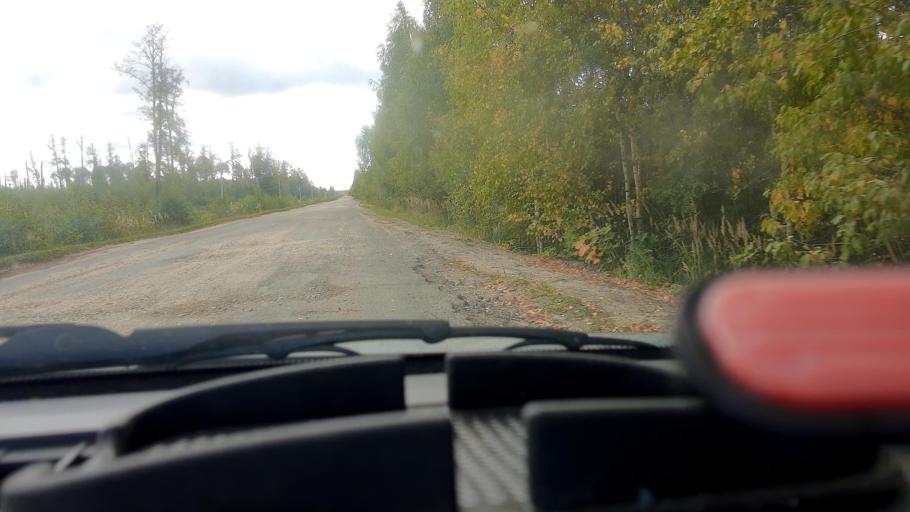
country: RU
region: Mariy-El
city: Kilemary
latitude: 56.8981
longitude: 46.7461
